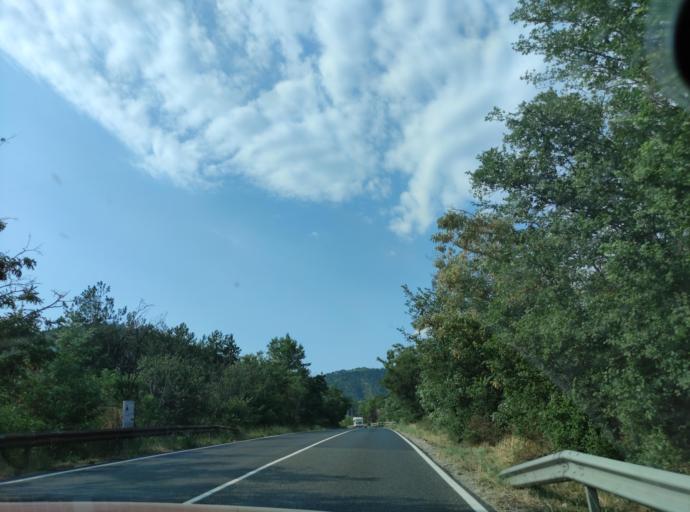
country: BG
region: Blagoevgrad
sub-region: Obshtina Kresna
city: Kresna
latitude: 41.7369
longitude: 23.1587
